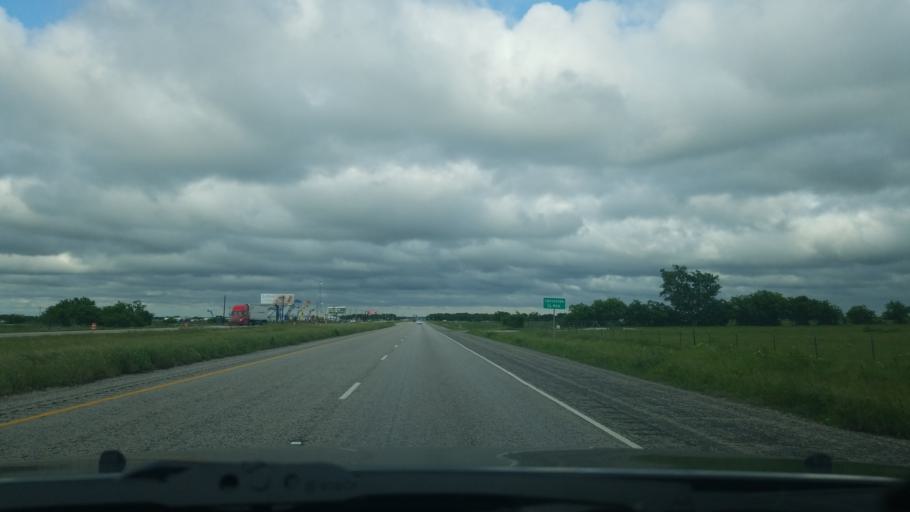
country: US
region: Texas
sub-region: Denton County
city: Ponder
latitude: 33.2390
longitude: -97.3333
